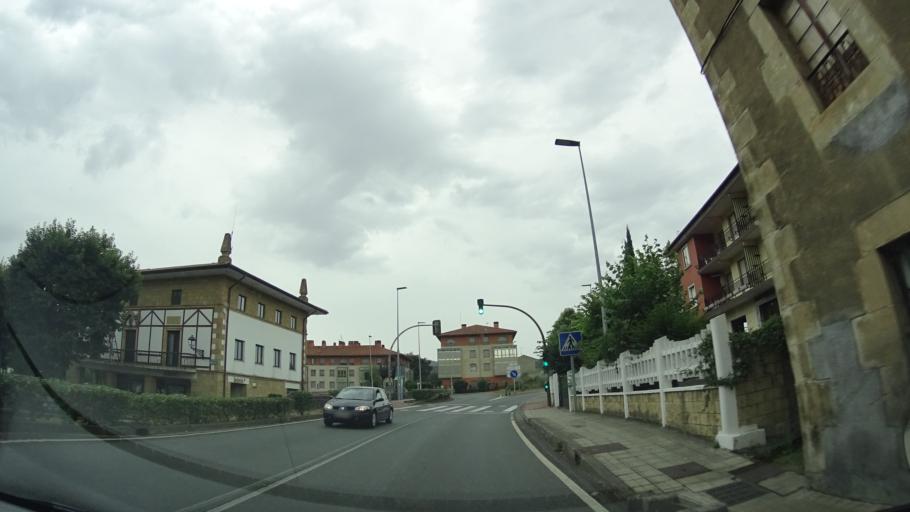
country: ES
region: Basque Country
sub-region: Bizkaia
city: Galdakao
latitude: 43.2086
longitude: -2.8019
